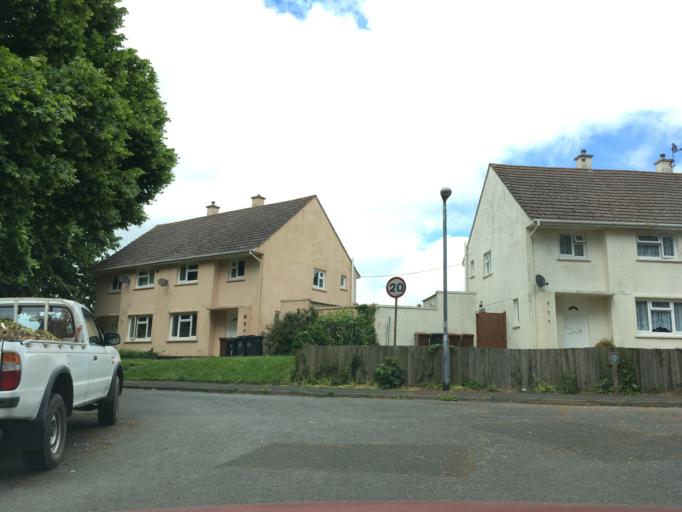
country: GB
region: England
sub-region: Devon
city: Dartmouth
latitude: 50.3532
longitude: -3.5920
